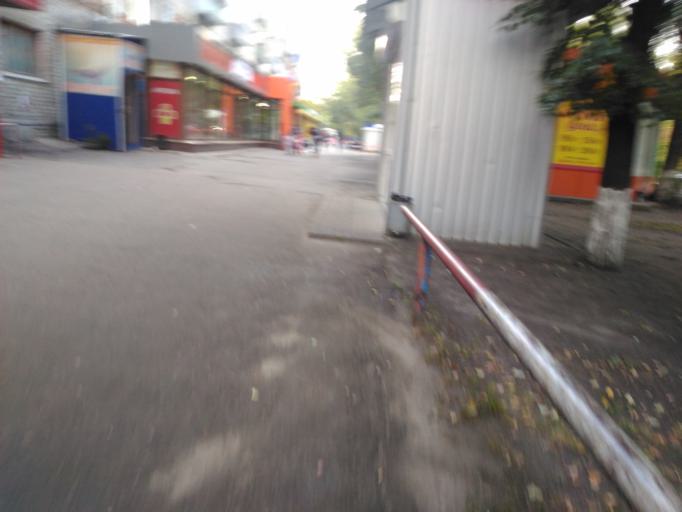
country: RU
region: Ulyanovsk
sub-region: Ulyanovskiy Rayon
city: Ulyanovsk
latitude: 54.3006
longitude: 48.3300
